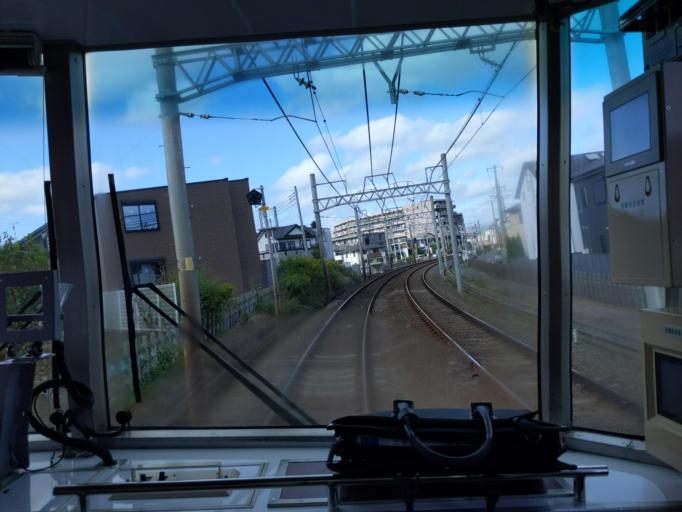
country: JP
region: Chiba
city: Funabashi
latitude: 35.7358
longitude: 140.0249
